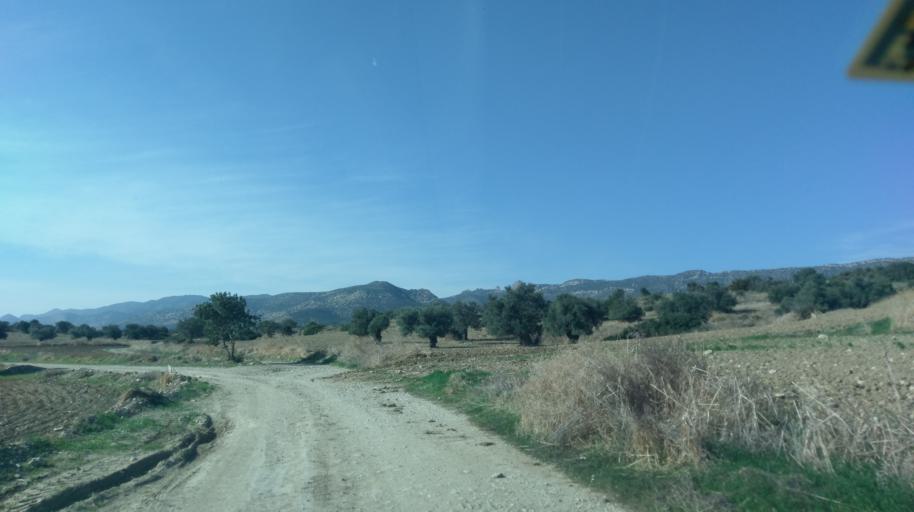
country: CY
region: Ammochostos
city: Trikomo
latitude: 35.3411
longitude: 33.8599
